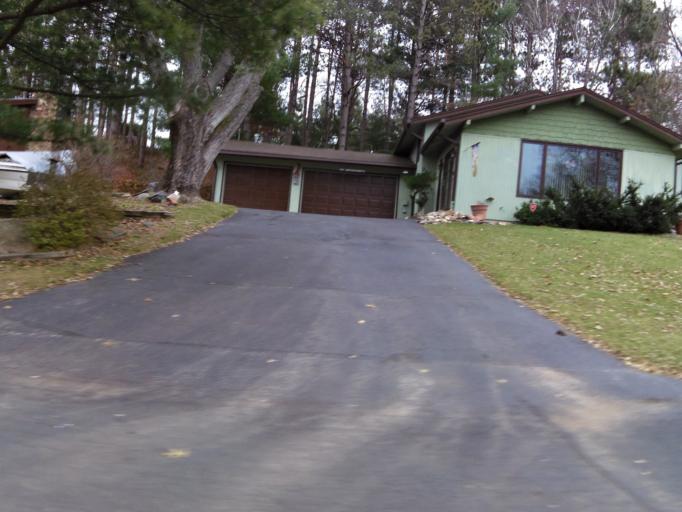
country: US
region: Minnesota
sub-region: Washington County
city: Lake Elmo
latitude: 44.9891
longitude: -92.8728
